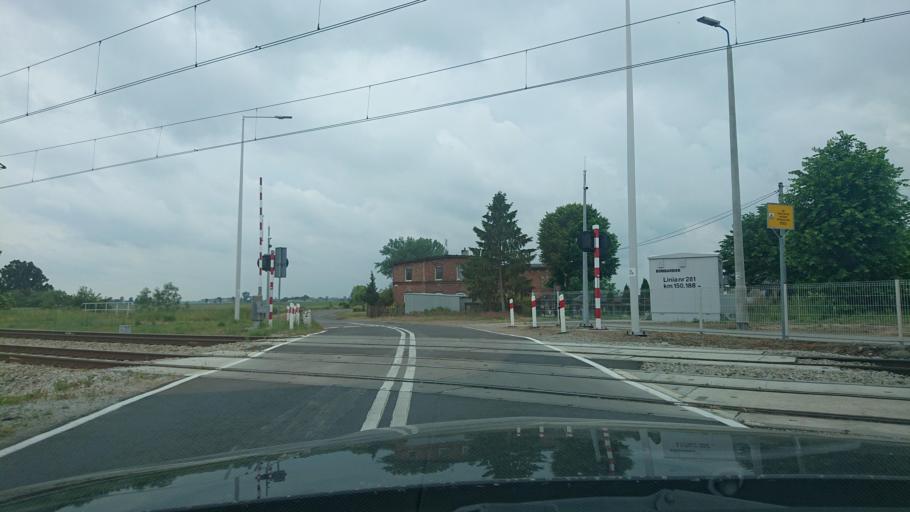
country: PL
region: Greater Poland Voivodeship
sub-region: Powiat gnieznienski
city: Gniezno
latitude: 52.4528
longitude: 17.5682
